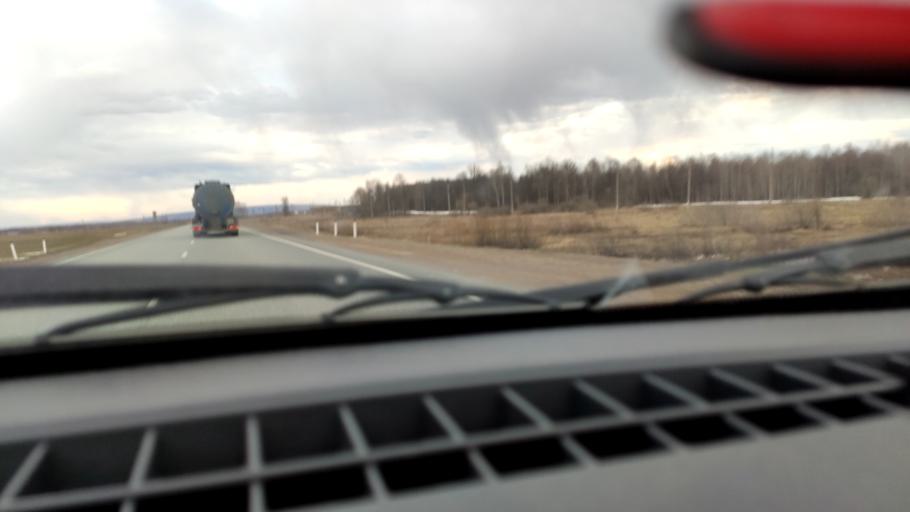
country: RU
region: Bashkortostan
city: Kudeyevskiy
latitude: 54.8168
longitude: 56.7438
